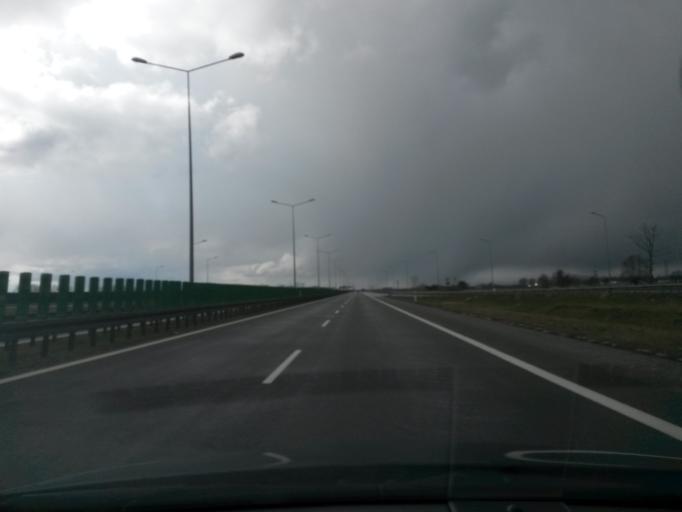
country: PL
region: Greater Poland Voivodeship
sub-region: Powiat poznanski
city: Kleszczewo
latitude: 52.3179
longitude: 17.1280
